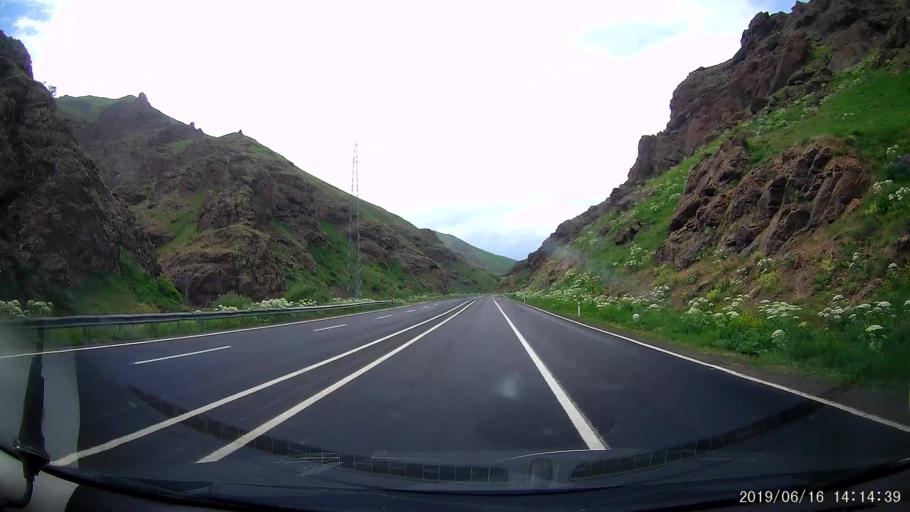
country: TR
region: Agri
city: Tahir
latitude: 39.7968
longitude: 42.4931
